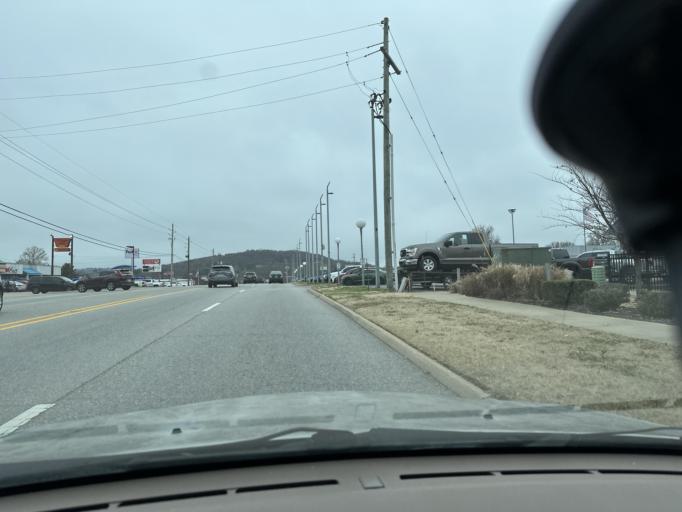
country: US
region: Arkansas
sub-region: Washington County
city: Johnson
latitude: 36.1129
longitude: -94.1452
